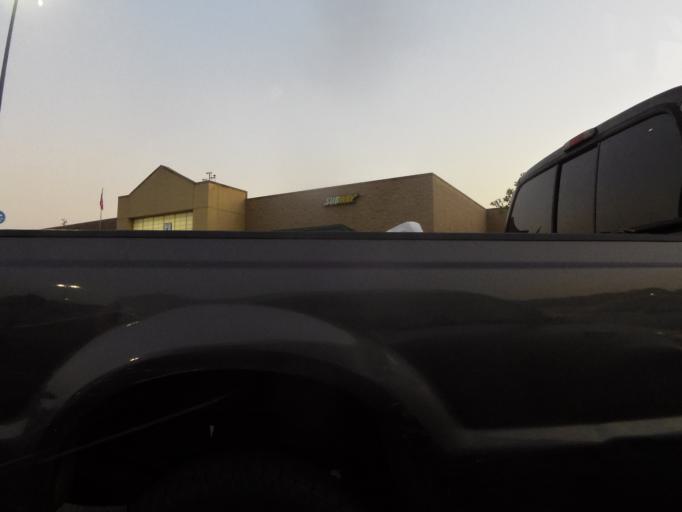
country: US
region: Florida
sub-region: Baker County
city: Macclenny
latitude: 30.2636
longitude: -82.1089
